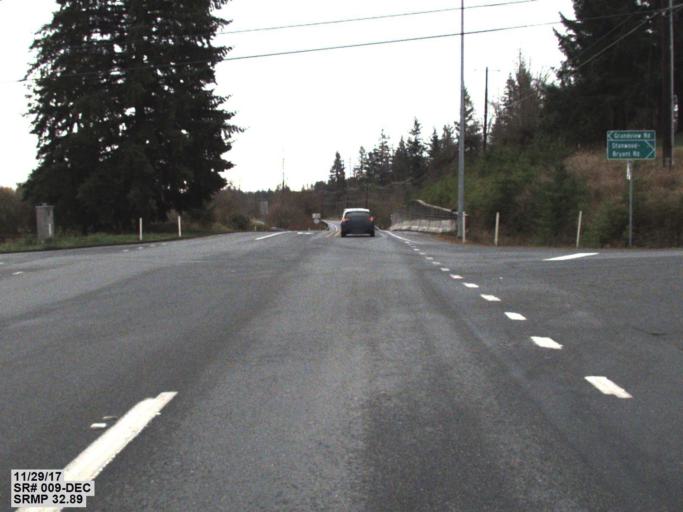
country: US
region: Washington
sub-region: Snohomish County
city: Bryant
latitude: 48.2391
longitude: -122.1589
